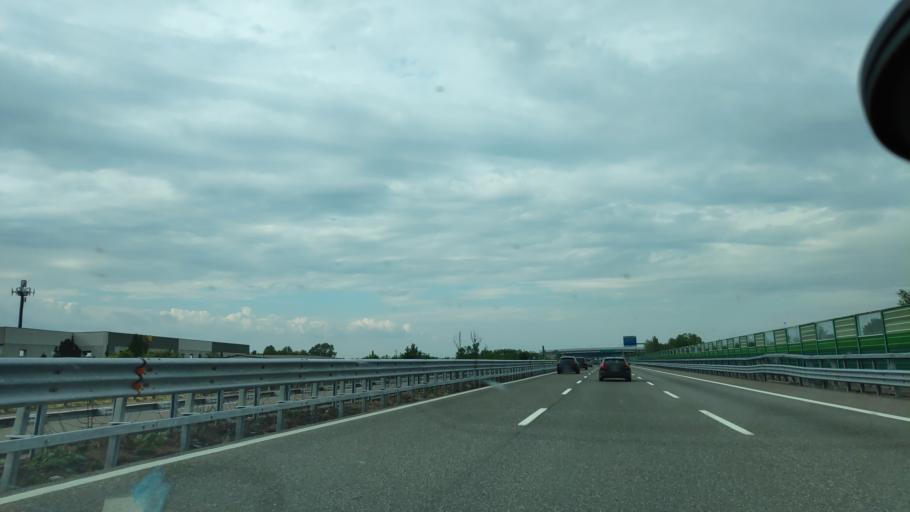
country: IT
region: Lombardy
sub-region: Provincia di Pavia
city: Casei
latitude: 45.0078
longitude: 8.9189
